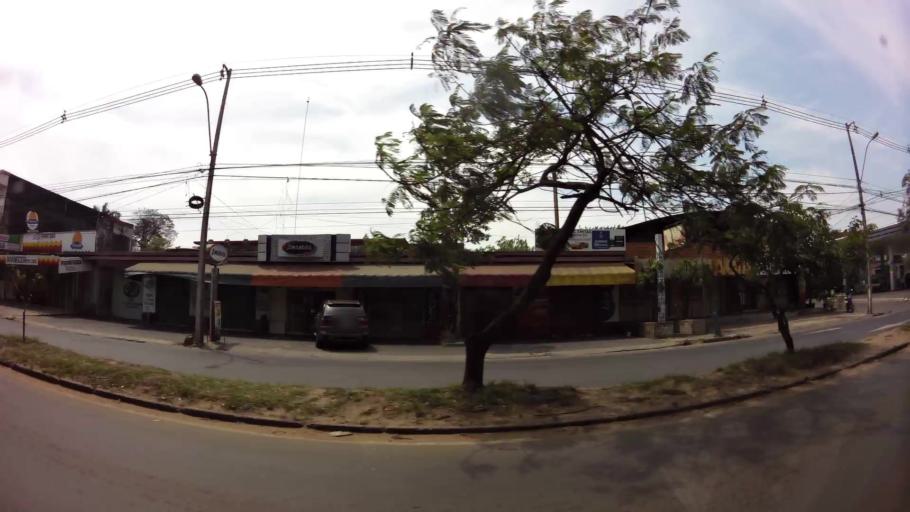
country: PY
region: Asuncion
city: Asuncion
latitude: -25.2668
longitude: -57.5829
